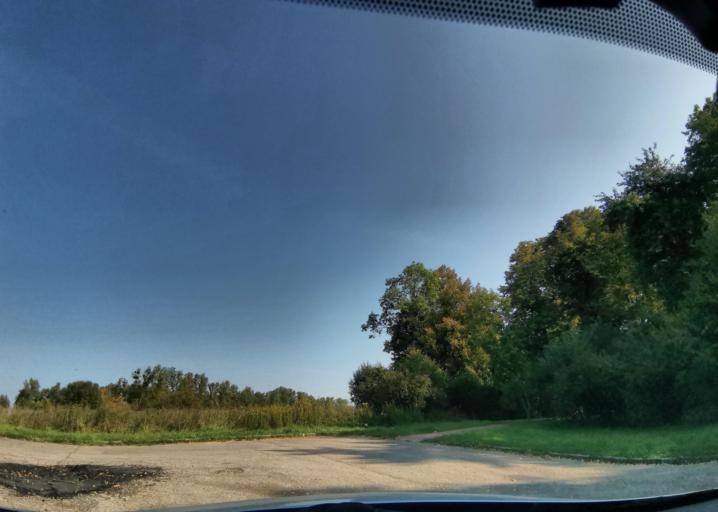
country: RU
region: Kaliningrad
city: Chernyakhovsk
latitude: 54.6920
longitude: 21.8559
